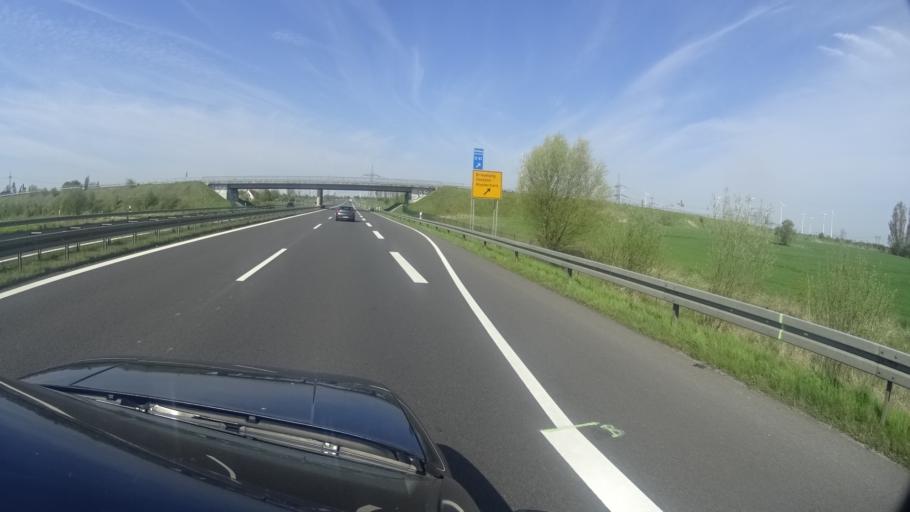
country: DE
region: Brandenburg
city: Wustermark
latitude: 52.5566
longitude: 12.9549
